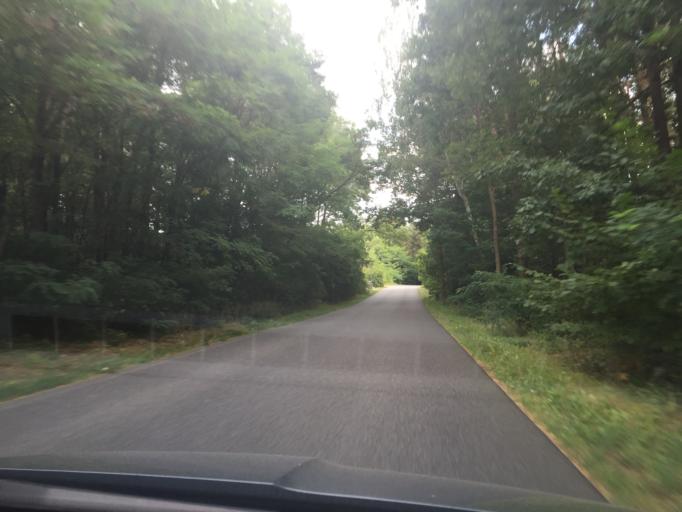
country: DE
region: Brandenburg
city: Spreenhagen
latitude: 52.3468
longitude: 13.8346
